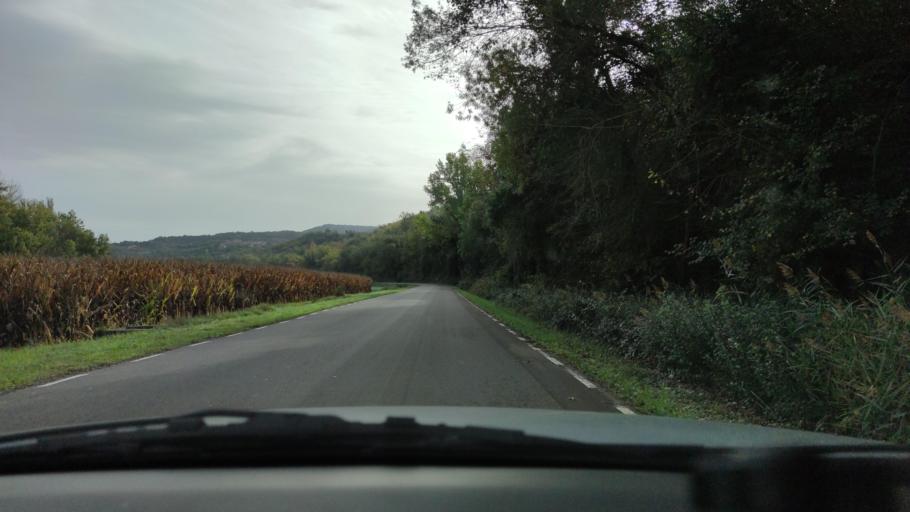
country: ES
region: Catalonia
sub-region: Provincia de Lleida
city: Artesa de Segre
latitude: 41.9181
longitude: 1.0963
